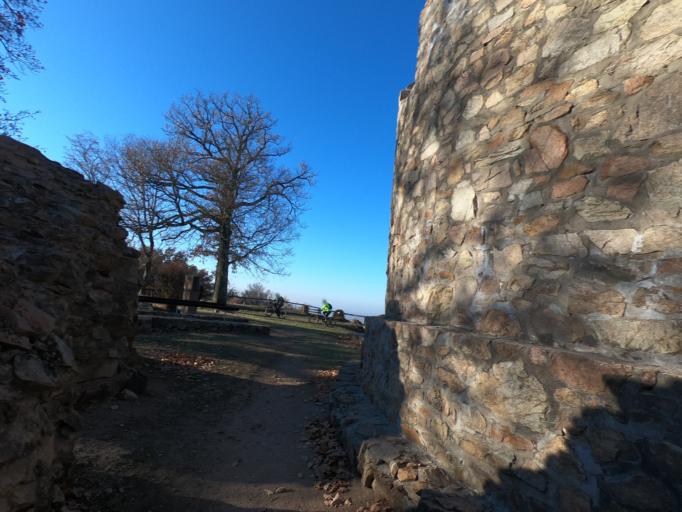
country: DE
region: Hesse
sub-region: Regierungsbezirk Darmstadt
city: Seeheim-Jugenheim
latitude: 49.7564
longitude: 8.6569
